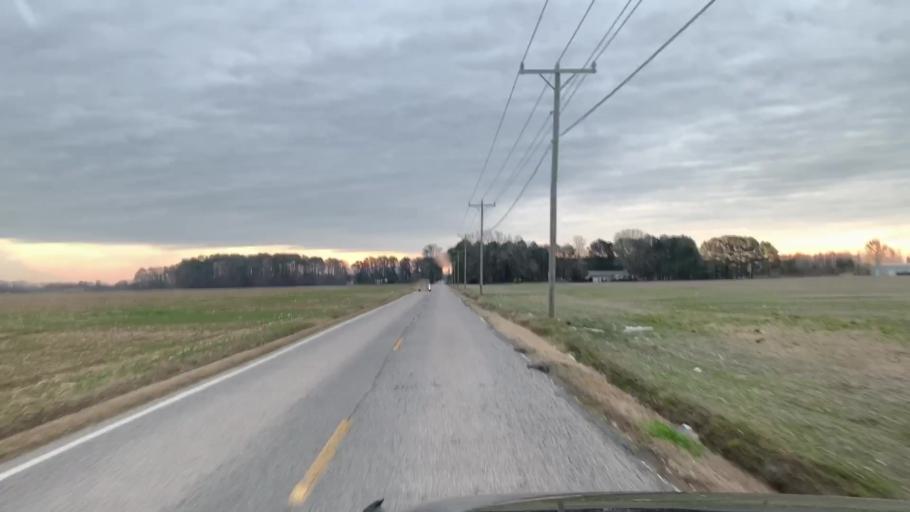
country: US
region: North Carolina
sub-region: Currituck County
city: Moyock
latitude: 36.6335
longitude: -76.1845
